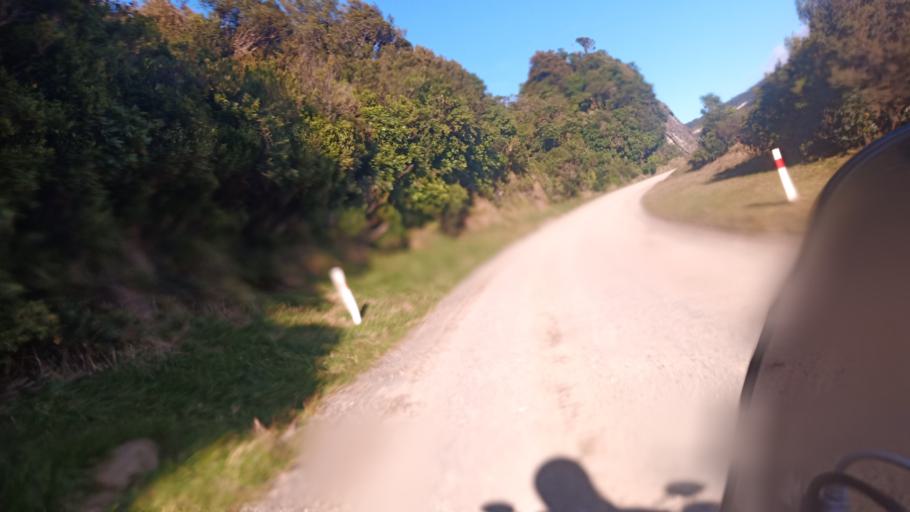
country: NZ
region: Hawke's Bay
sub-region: Wairoa District
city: Wairoa
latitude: -38.7876
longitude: 177.1304
